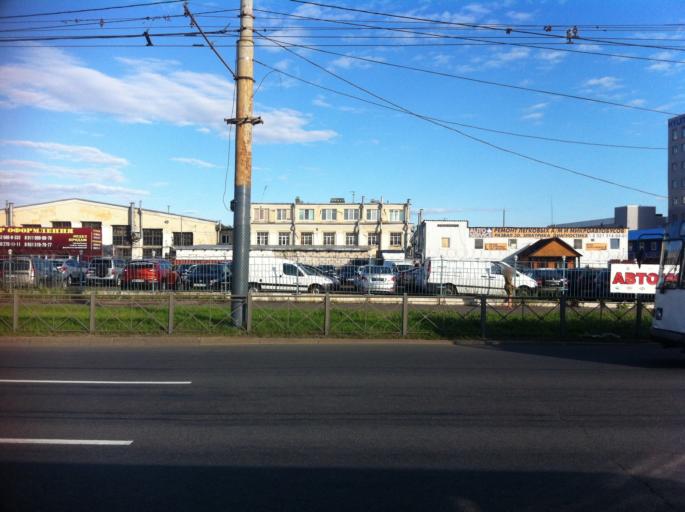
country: RU
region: St.-Petersburg
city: Avtovo
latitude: 59.8681
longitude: 30.2450
